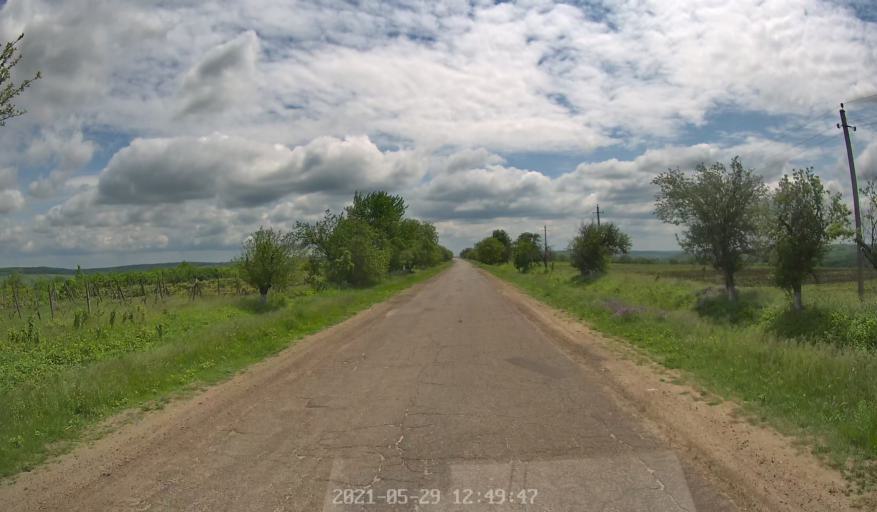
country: MD
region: Hincesti
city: Hincesti
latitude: 46.8486
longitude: 28.6520
